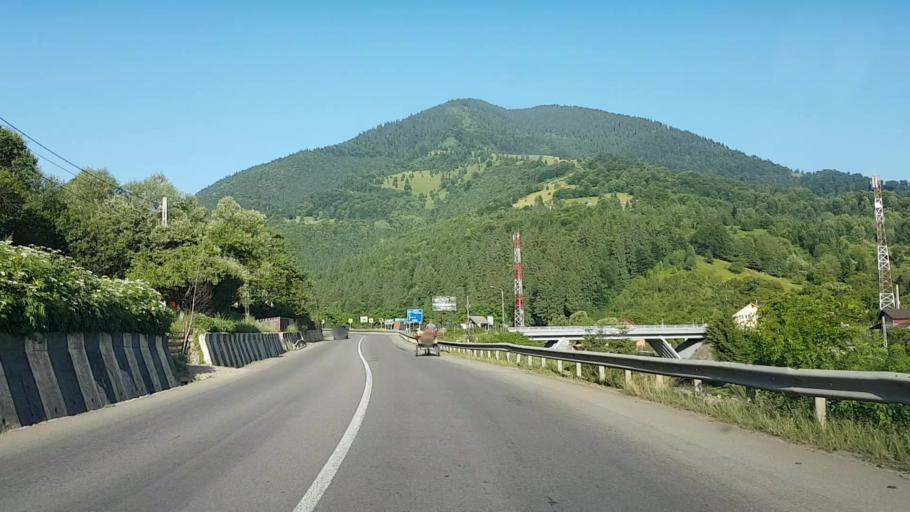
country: RO
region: Bistrita-Nasaud
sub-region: Comuna Tiha Bargaului
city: Tureac
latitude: 47.2097
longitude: 24.8670
